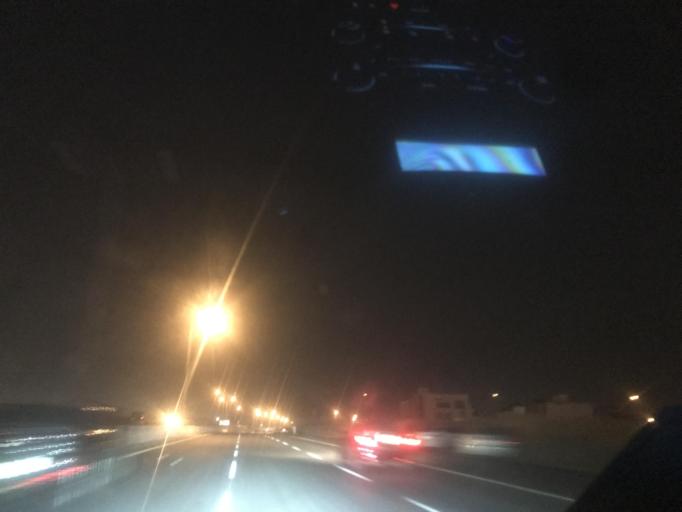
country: SA
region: Ar Riyad
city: Riyadh
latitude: 24.7665
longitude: 46.5969
